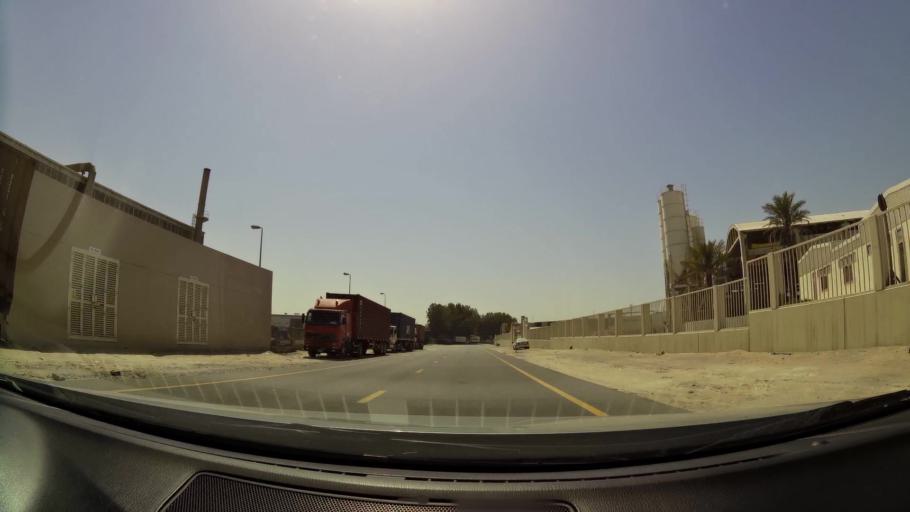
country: AE
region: Dubai
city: Dubai
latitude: 24.9691
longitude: 55.1763
